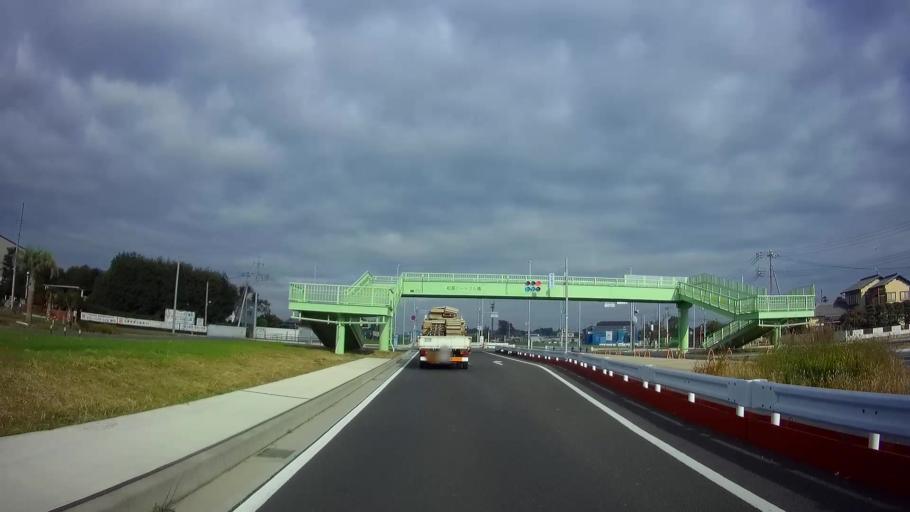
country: JP
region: Saitama
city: Okegawa
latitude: 35.9844
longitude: 139.5329
